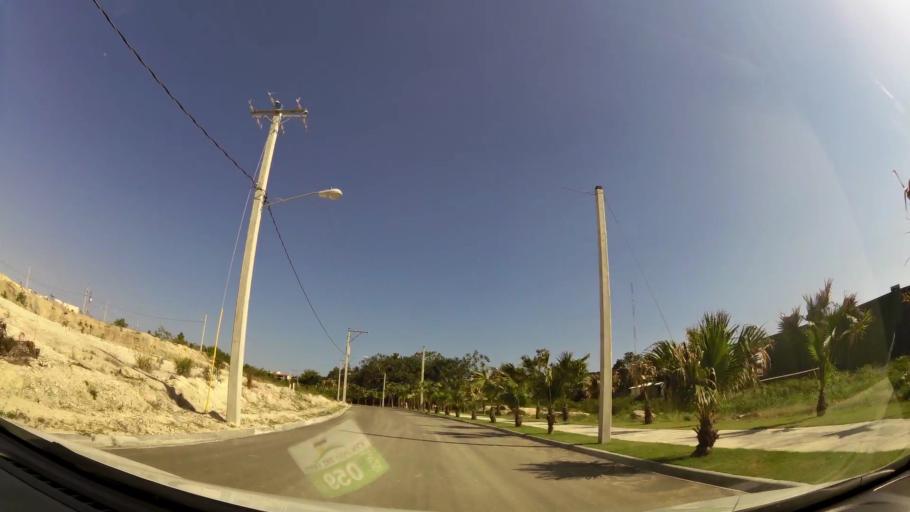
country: DO
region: Nacional
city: Santo Domingo
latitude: 18.4616
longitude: -69.9869
